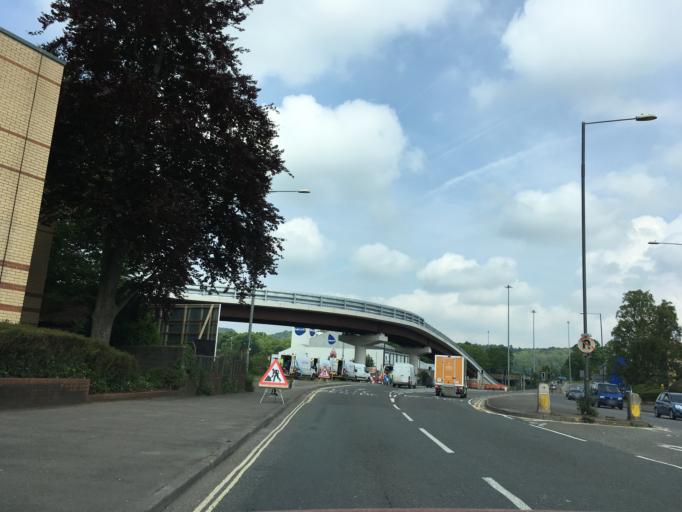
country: GB
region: England
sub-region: Bristol
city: Bristol
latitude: 51.4386
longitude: -2.6227
